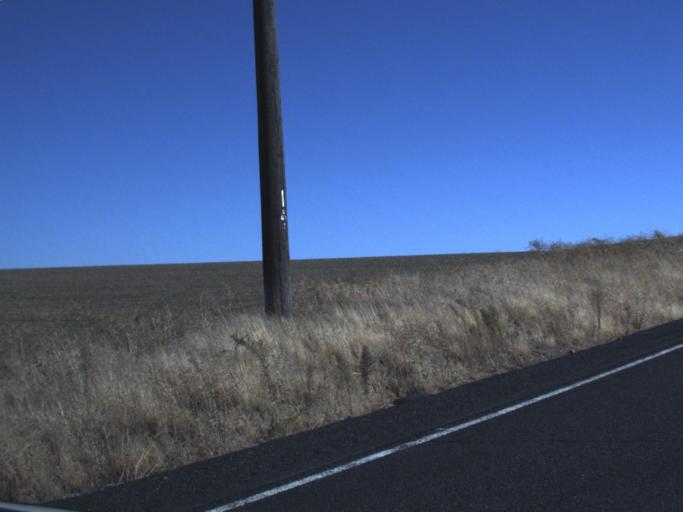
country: US
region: Washington
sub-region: Adams County
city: Ritzville
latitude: 46.8744
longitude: -118.5539
